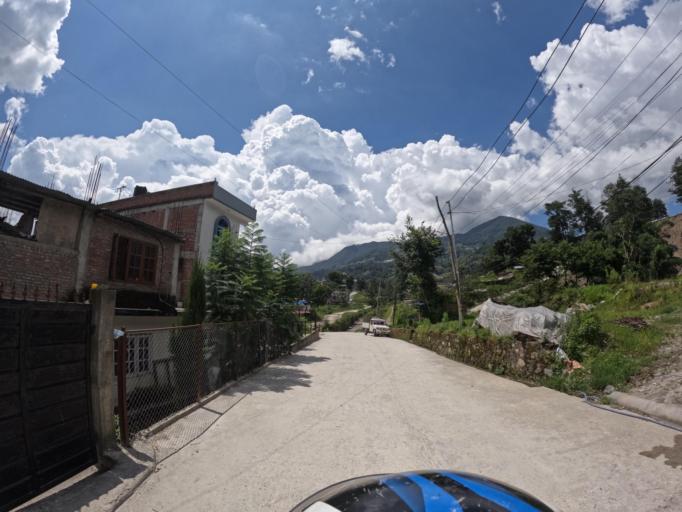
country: NP
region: Central Region
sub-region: Bagmati Zone
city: Kathmandu
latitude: 27.7863
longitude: 85.3264
